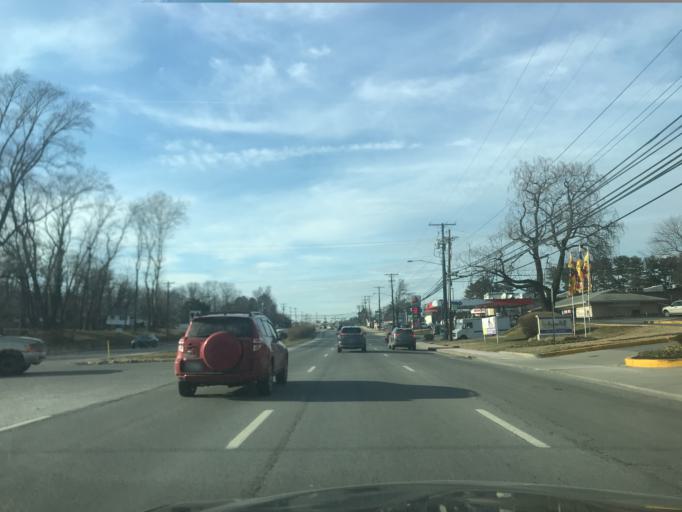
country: US
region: Maryland
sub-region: Montgomery County
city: Aspen Hill
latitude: 39.0781
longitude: -77.0714
